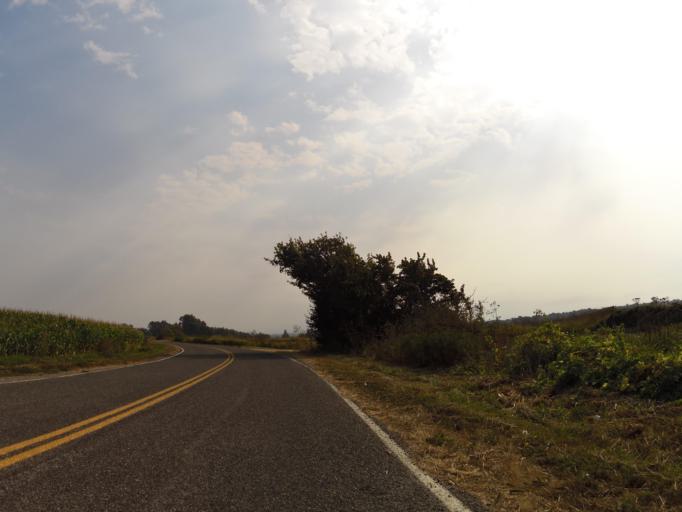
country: US
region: Washington
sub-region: Whatcom County
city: Ferndale
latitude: 48.8080
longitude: -122.6392
